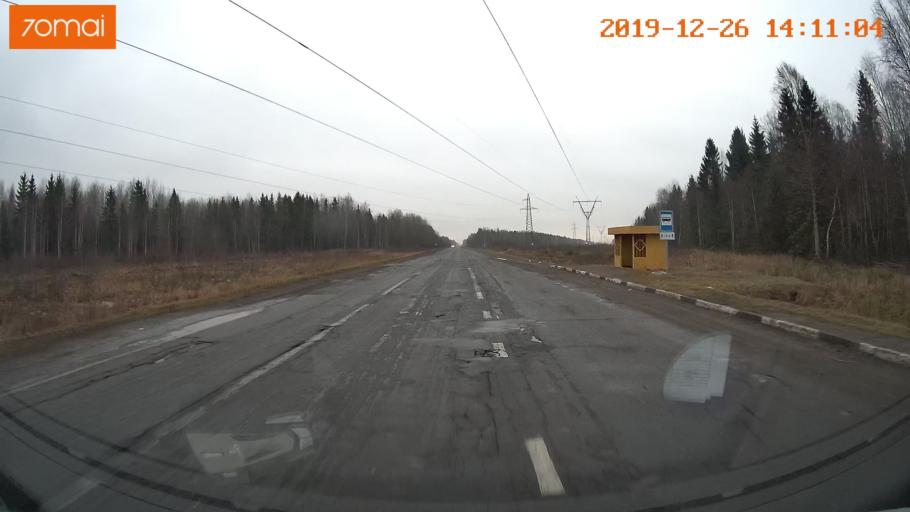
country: RU
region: Jaroslavl
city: Poshekhon'ye
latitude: 58.5090
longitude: 38.9661
